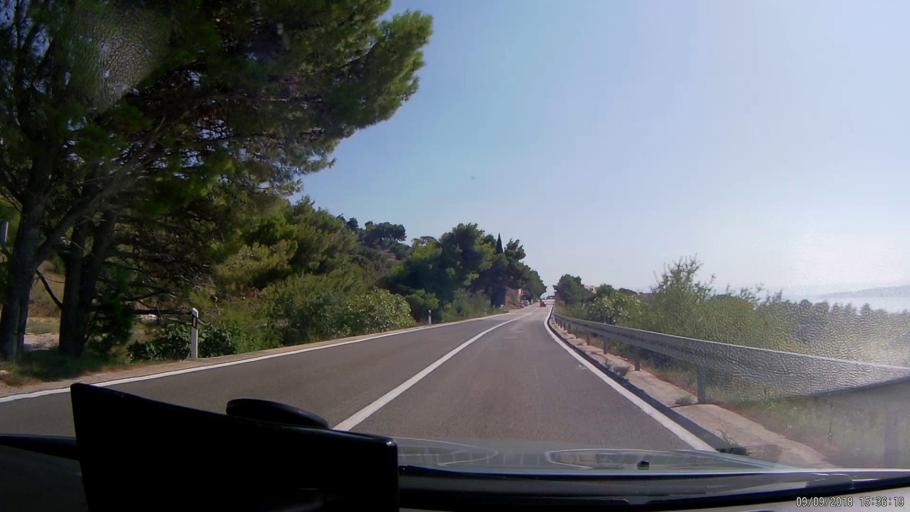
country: HR
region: Splitsko-Dalmatinska
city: Donja Brela
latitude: 43.3792
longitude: 16.9225
